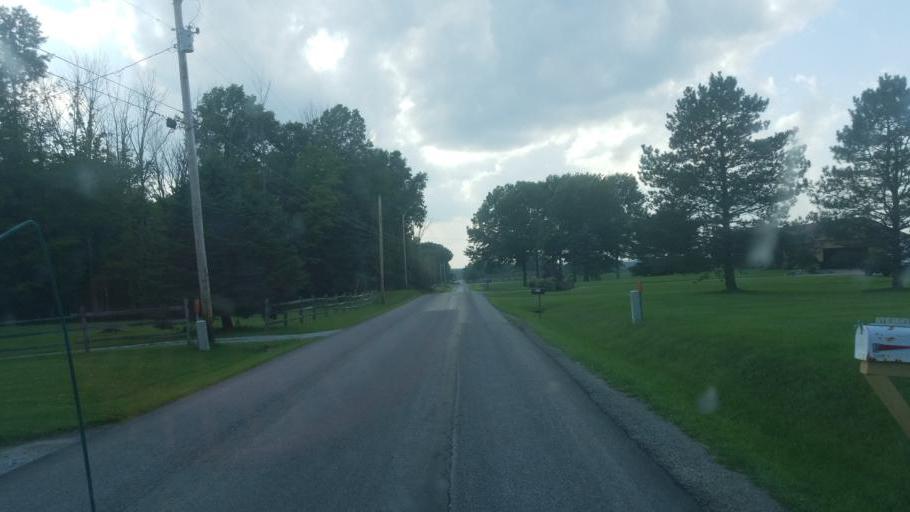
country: US
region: Ohio
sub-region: Wayne County
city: West Salem
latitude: 40.9522
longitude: -82.0804
